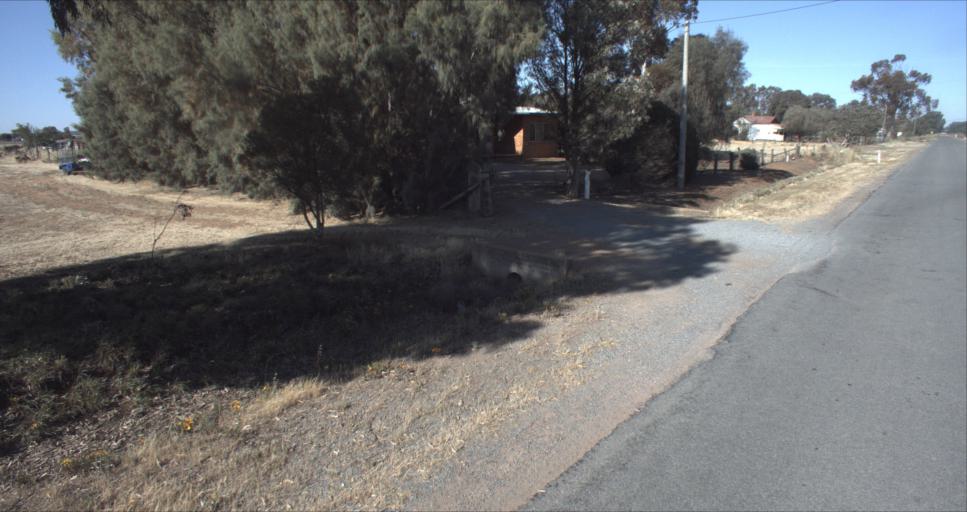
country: AU
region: New South Wales
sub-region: Leeton
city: Leeton
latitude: -34.5402
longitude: 146.4114
